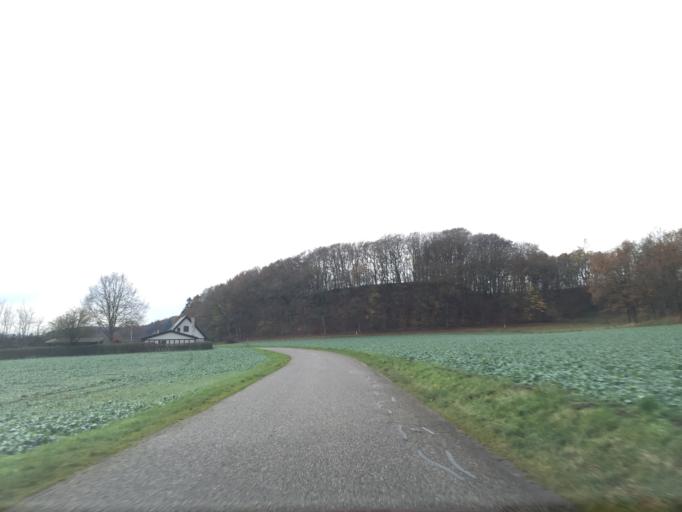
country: DK
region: Central Jutland
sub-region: Skanderborg Kommune
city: Ry
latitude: 56.1582
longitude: 9.7403
